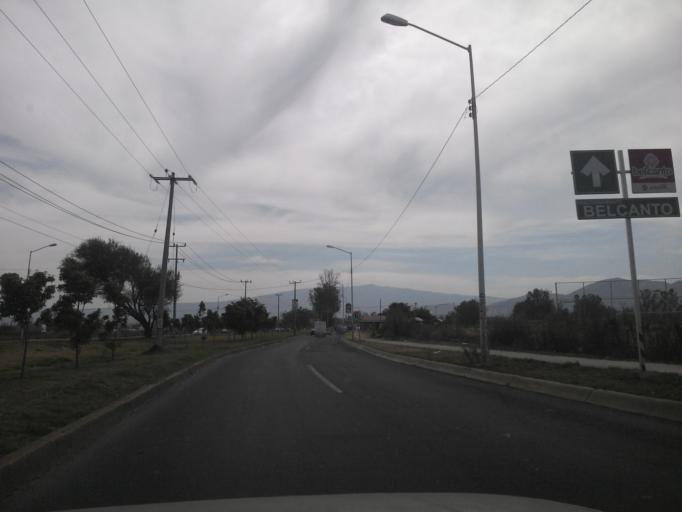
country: MX
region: Jalisco
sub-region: San Pedro Tlaquepaque
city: Paseo del Prado
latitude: 20.5697
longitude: -103.3915
